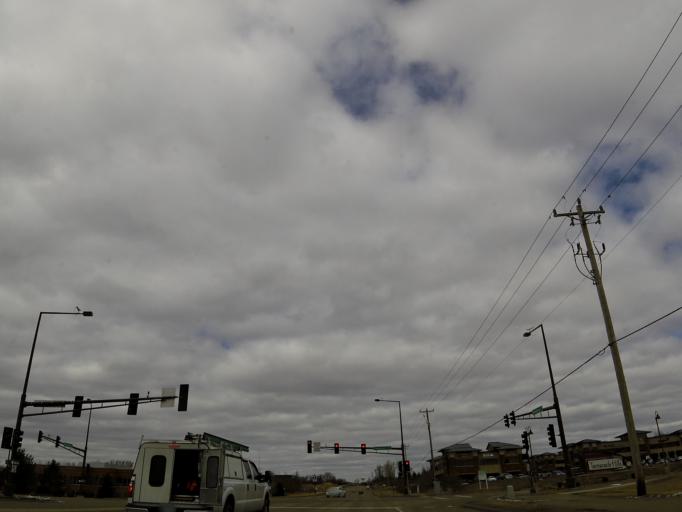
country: US
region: Minnesota
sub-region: Washington County
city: Woodbury
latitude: 44.9386
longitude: -92.9542
